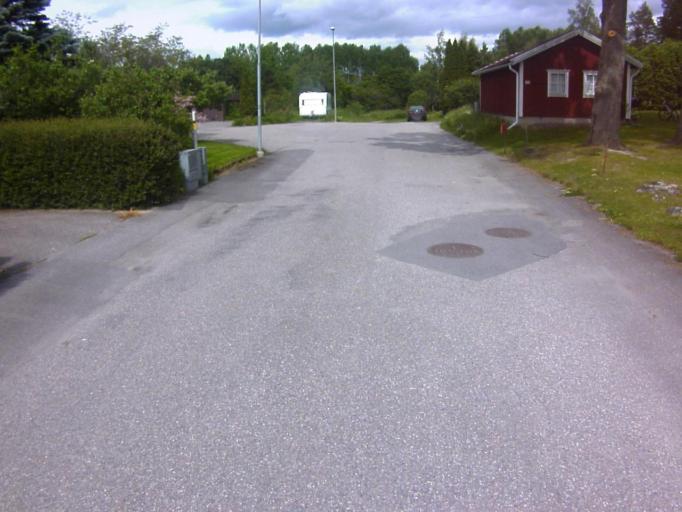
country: SE
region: Soedermanland
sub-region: Eskilstuna Kommun
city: Skogstorp
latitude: 59.3196
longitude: 16.4951
